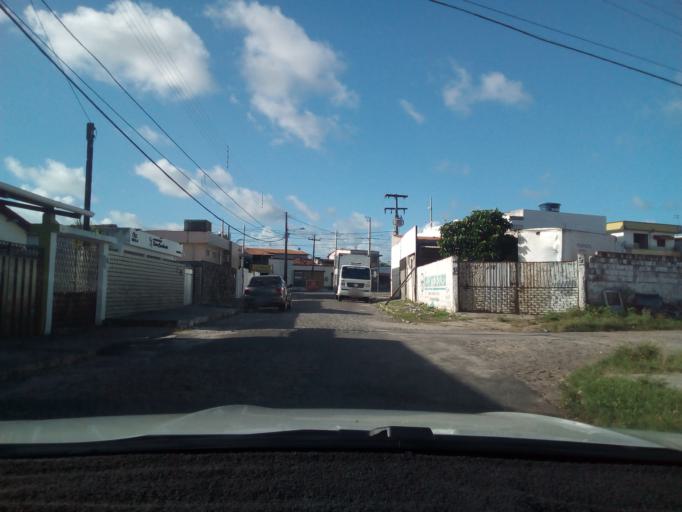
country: BR
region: Paraiba
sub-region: Joao Pessoa
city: Joao Pessoa
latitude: -7.1729
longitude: -34.8431
